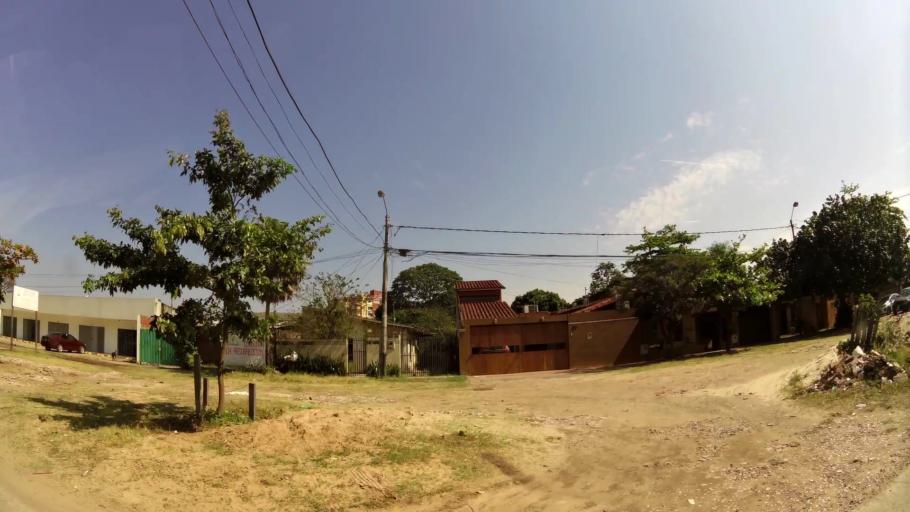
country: BO
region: Santa Cruz
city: Santa Cruz de la Sierra
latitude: -17.7436
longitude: -63.1713
